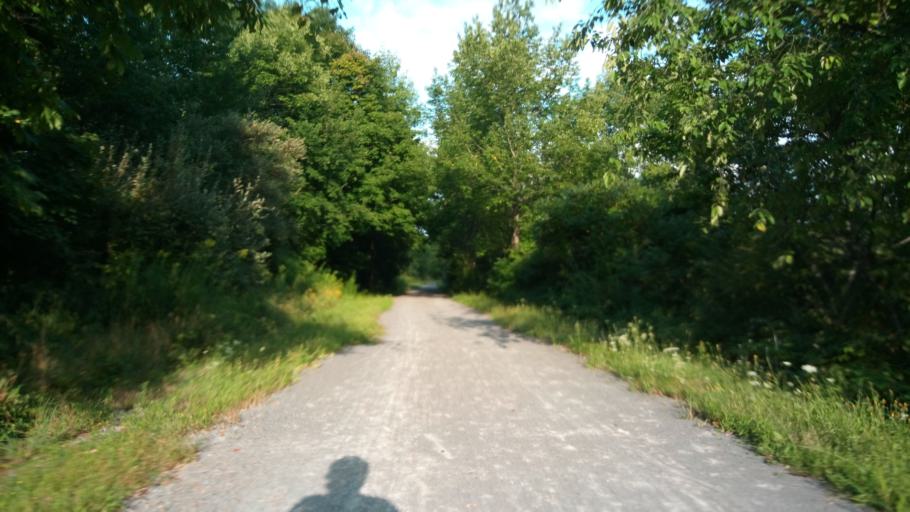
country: US
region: New York
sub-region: Ontario County
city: Victor
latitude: 43.0005
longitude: -77.4487
